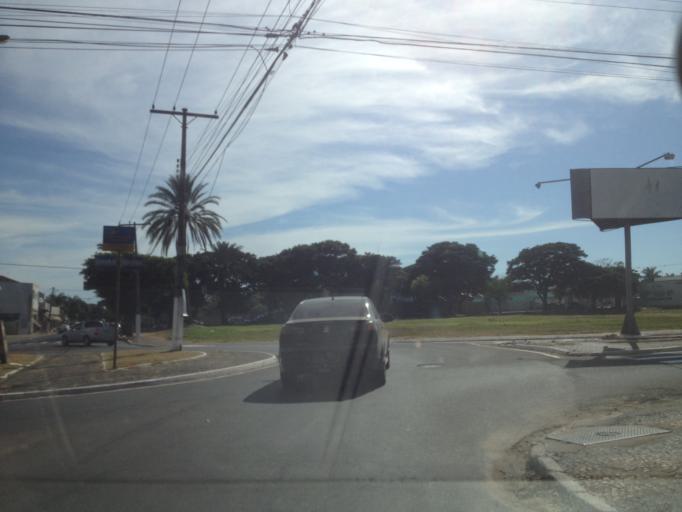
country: BR
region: Sao Paulo
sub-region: Marilia
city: Marilia
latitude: -22.2163
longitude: -49.9397
